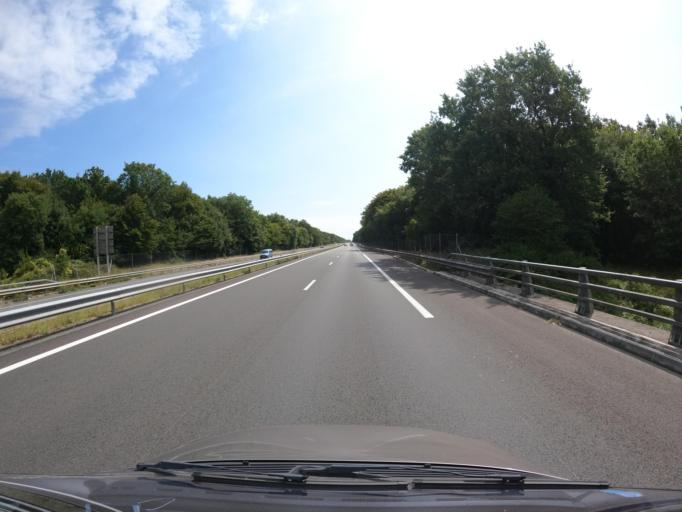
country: FR
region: Poitou-Charentes
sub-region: Departement de la Charente-Maritime
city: Courcon
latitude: 46.2196
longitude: -0.7955
